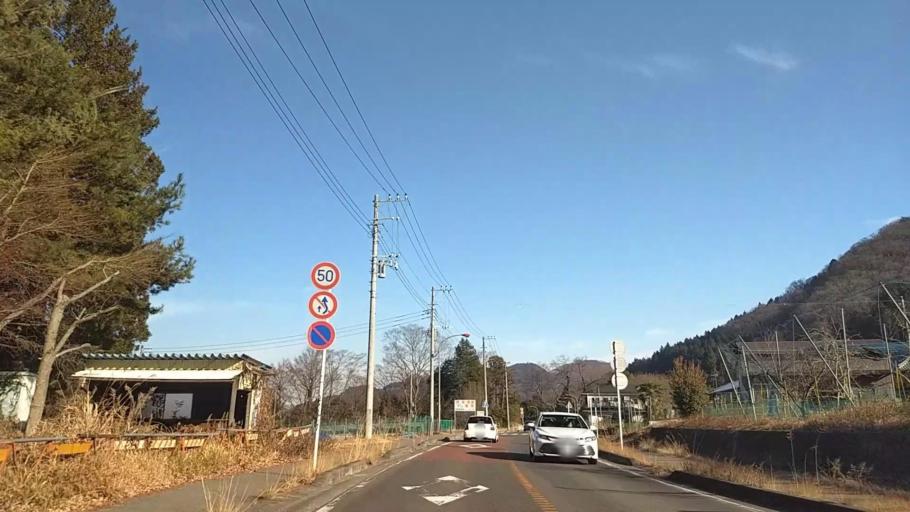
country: JP
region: Yamanashi
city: Uenohara
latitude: 35.5608
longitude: 139.1807
